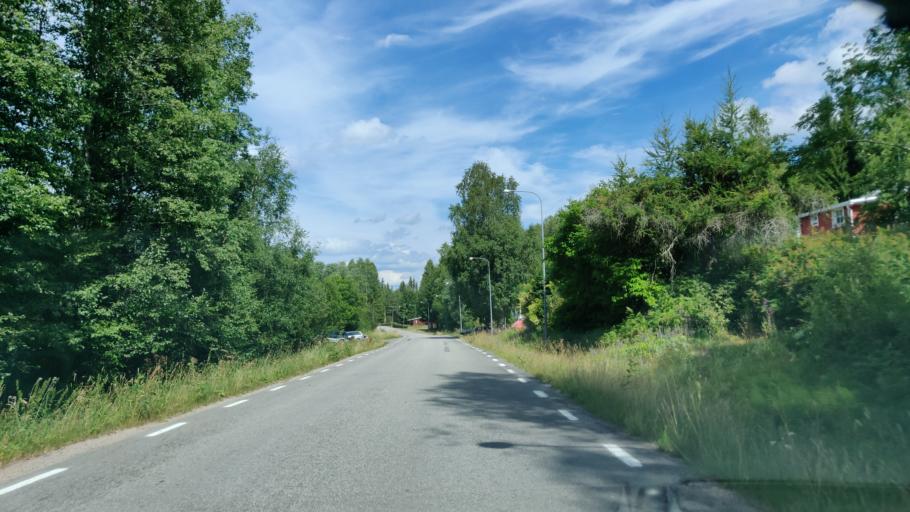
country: SE
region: Vaermland
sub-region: Hagfors Kommun
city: Ekshaerad
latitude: 60.1085
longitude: 13.5011
